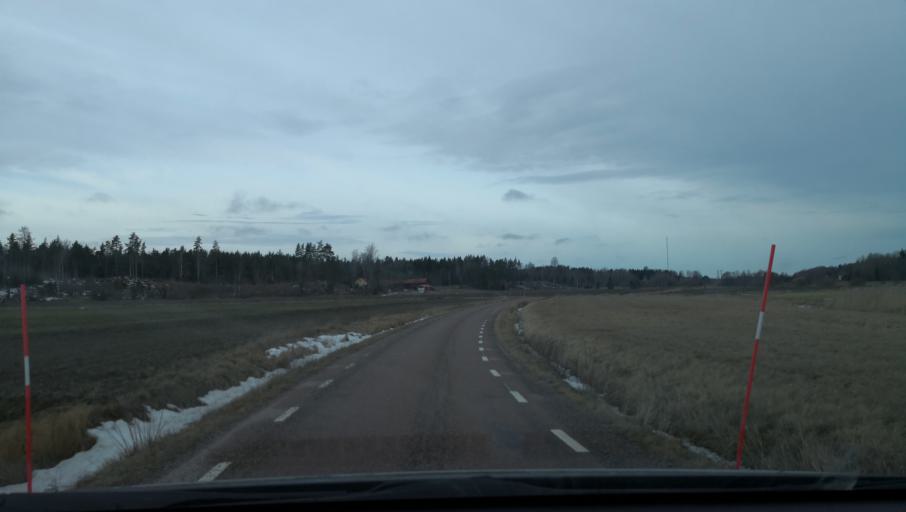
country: SE
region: Vaestmanland
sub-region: Vasteras
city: Skultuna
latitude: 59.6004
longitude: 16.4130
